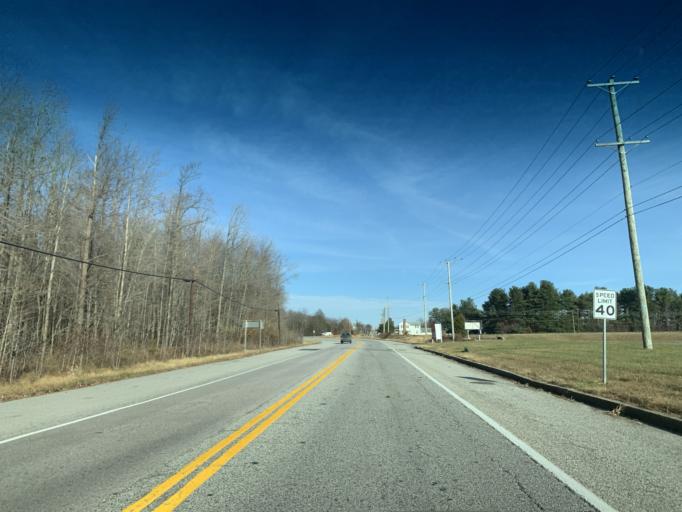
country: US
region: Maryland
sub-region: Cecil County
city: Perryville
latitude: 39.5637
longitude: -76.0635
